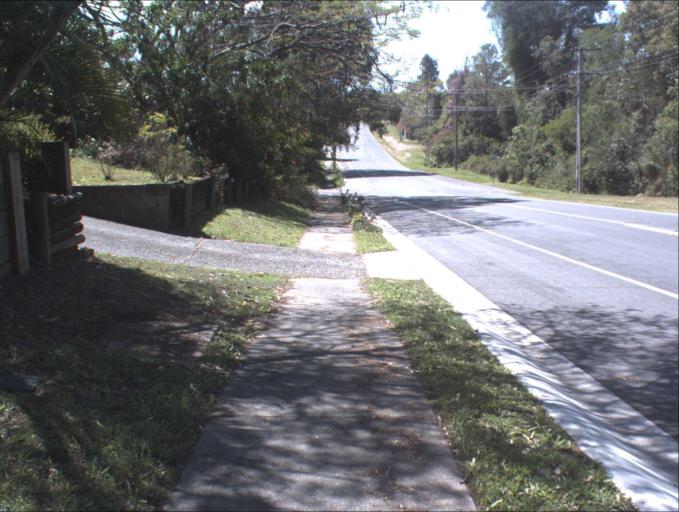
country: AU
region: Queensland
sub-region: Logan
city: Beenleigh
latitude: -27.7076
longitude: 153.1816
